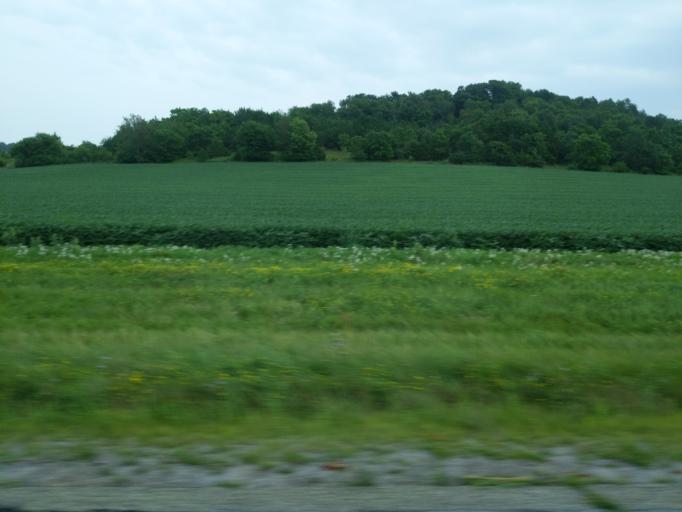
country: US
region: Wisconsin
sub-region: Dane County
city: Mazomanie
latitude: 43.1890
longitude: -89.7592
